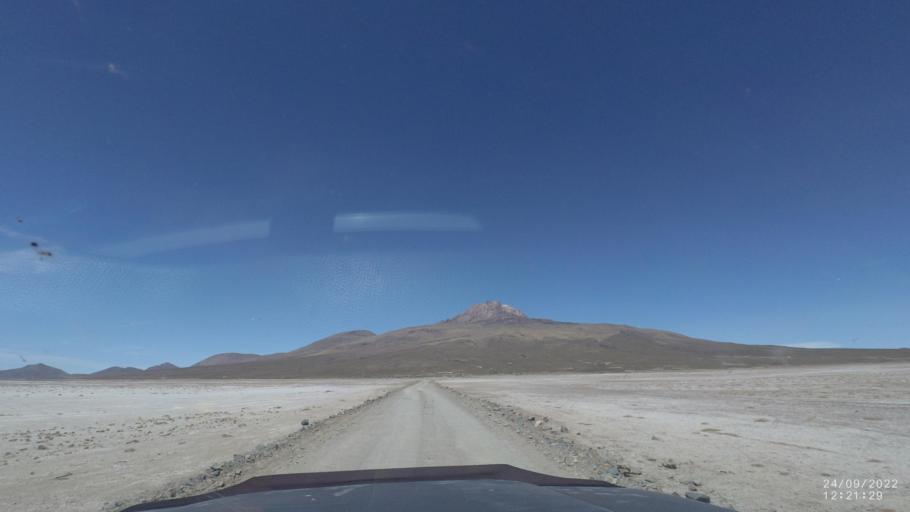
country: BO
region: Potosi
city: Colchani
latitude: -19.7488
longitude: -67.6688
